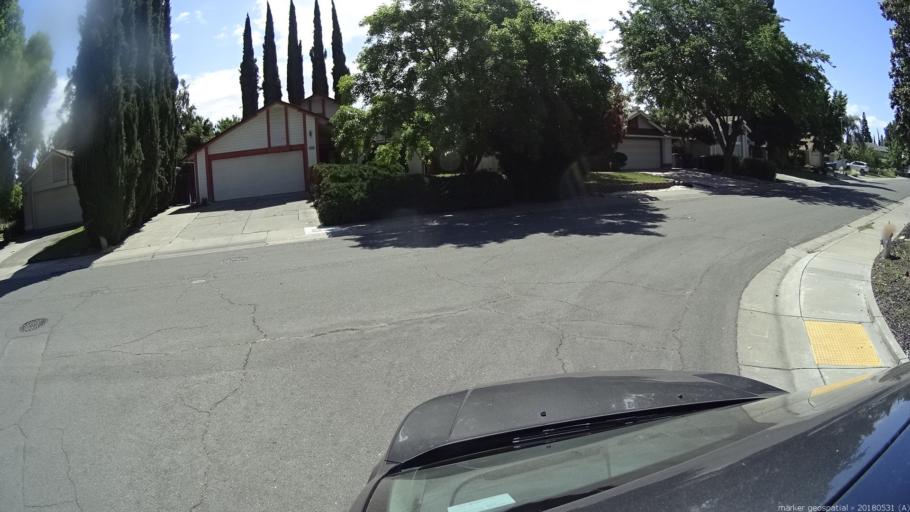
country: US
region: California
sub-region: Sacramento County
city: Sacramento
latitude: 38.6236
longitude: -121.4953
